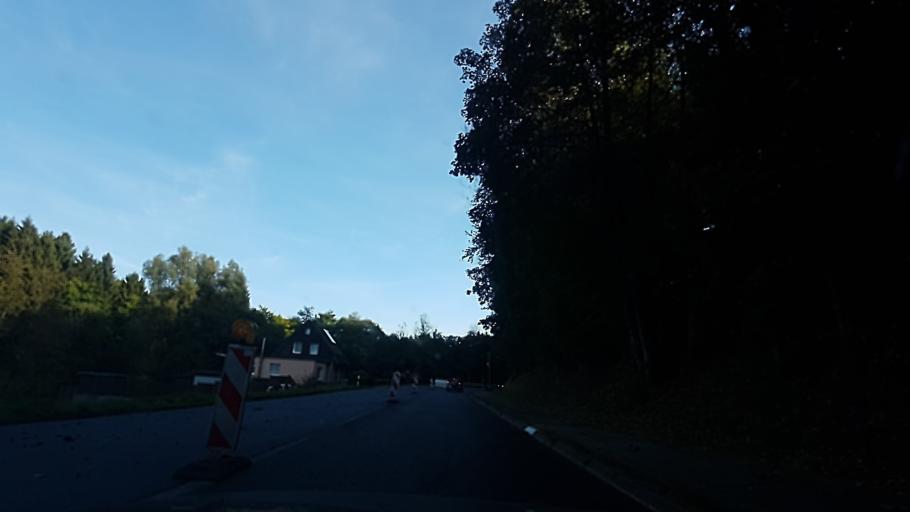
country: DE
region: North Rhine-Westphalia
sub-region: Regierungsbezirk Koln
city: Marienheide
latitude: 51.0920
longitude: 7.5264
